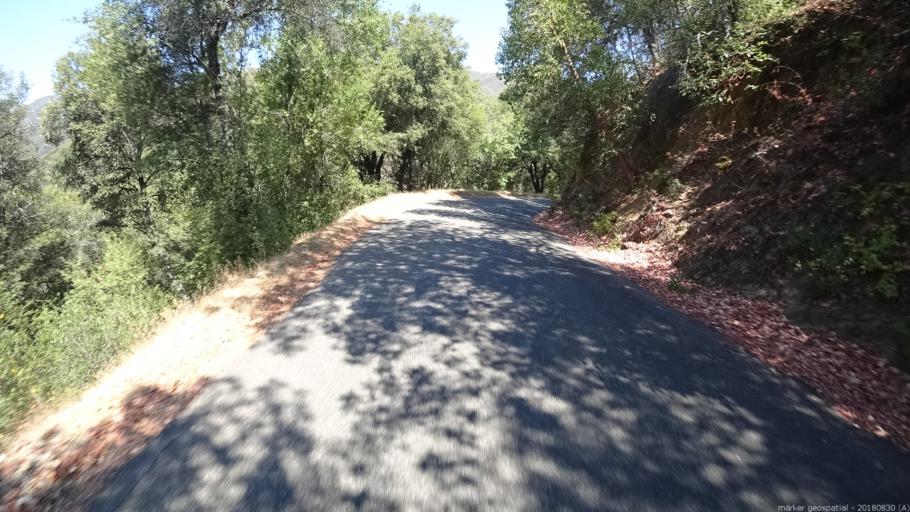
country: US
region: California
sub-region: Monterey County
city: Greenfield
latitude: 36.0152
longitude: -121.4311
